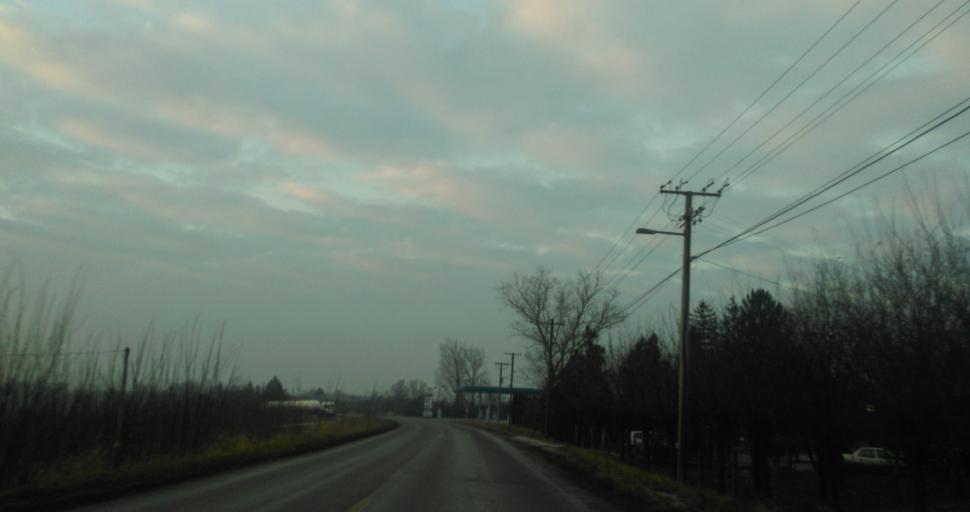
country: RS
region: Autonomna Pokrajina Vojvodina
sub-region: Juznobacki Okrug
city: Becej
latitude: 45.6462
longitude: 20.0312
